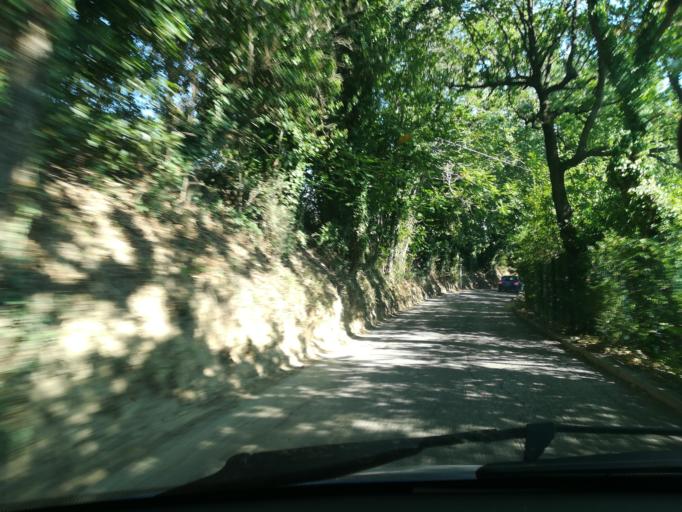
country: IT
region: The Marches
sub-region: Provincia di Macerata
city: Piediripa
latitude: 43.2956
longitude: 13.4839
